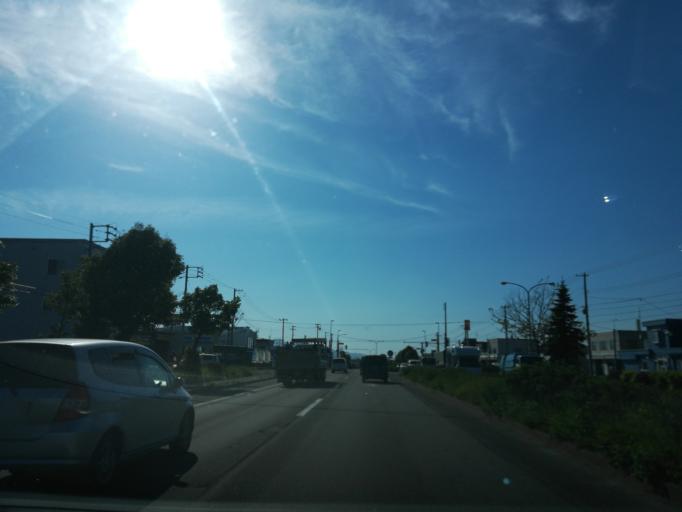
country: JP
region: Hokkaido
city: Kitahiroshima
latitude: 43.0138
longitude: 141.5029
